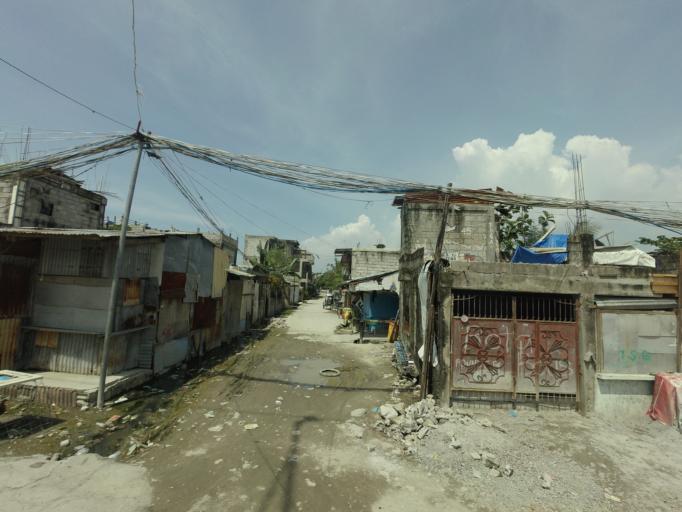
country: PH
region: Calabarzon
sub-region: Province of Rizal
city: Taytay
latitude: 14.5348
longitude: 121.1110
